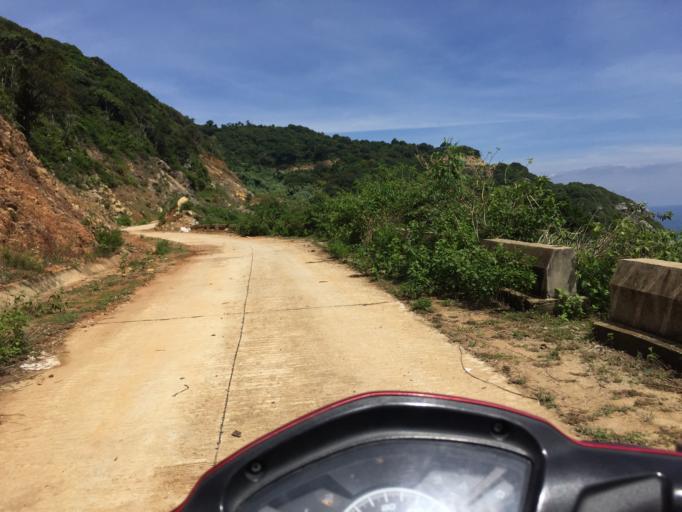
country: VN
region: Quang Nam
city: Hoi An
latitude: 15.9679
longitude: 108.5083
